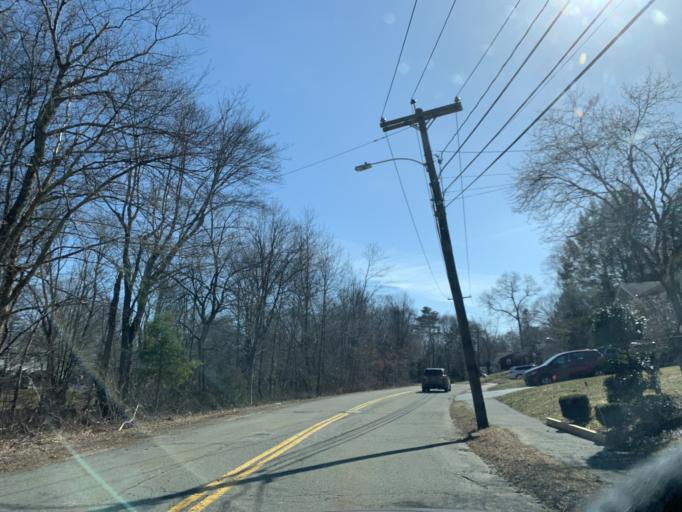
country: US
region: Massachusetts
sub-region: Norfolk County
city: Westwood
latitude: 42.1918
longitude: -71.2230
